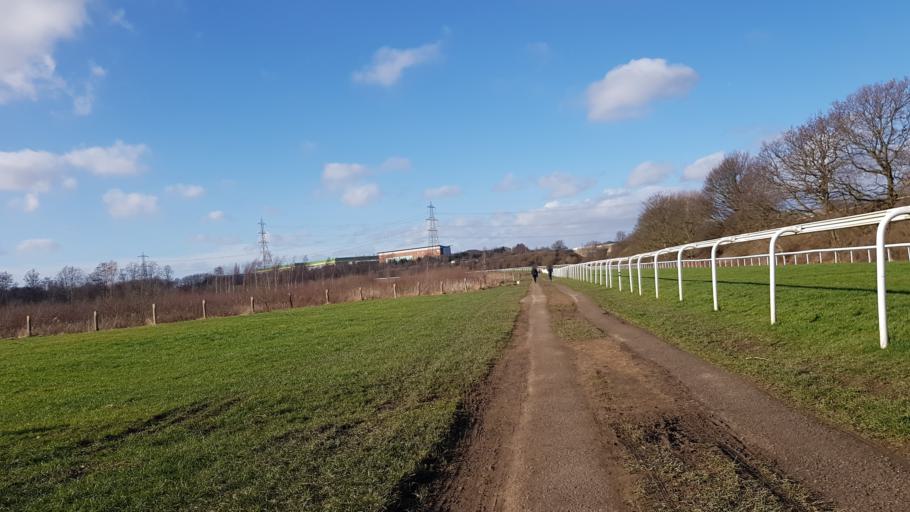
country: GB
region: England
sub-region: City and Borough of Wakefield
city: Pontefract
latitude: 53.7047
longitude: -1.3302
